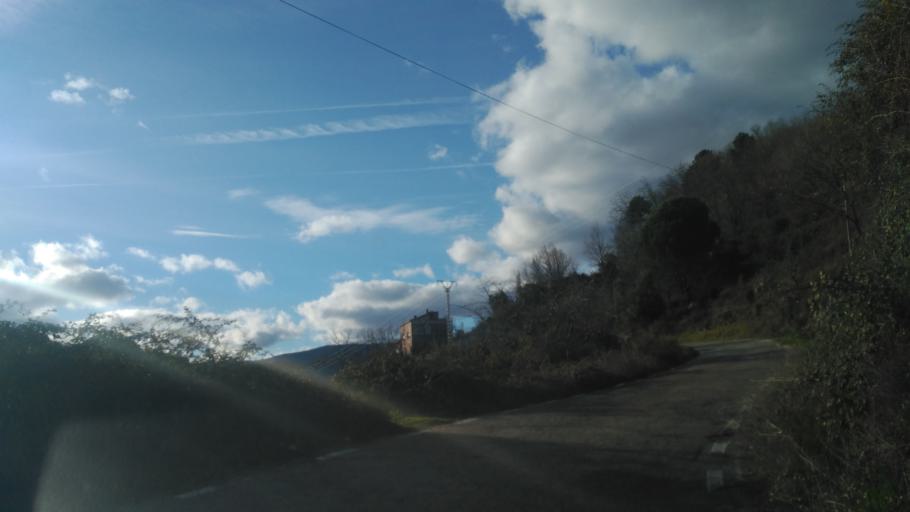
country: ES
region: Castille and Leon
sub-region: Provincia de Salamanca
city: Sequeros
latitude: 40.5079
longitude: -6.0406
